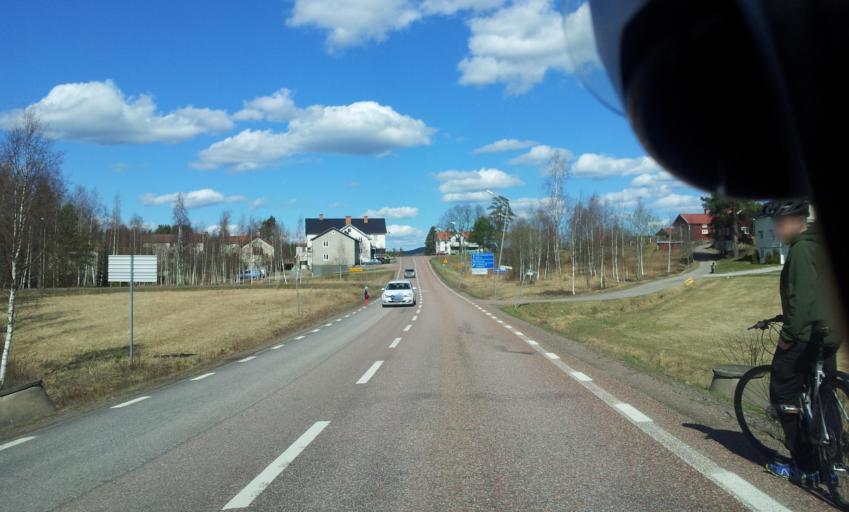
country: SE
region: Dalarna
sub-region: Faluns Kommun
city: Svardsjo
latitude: 60.8059
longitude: 15.7569
